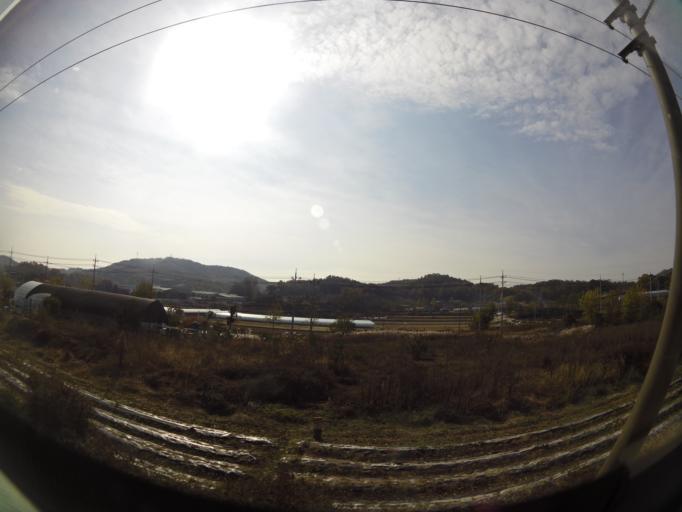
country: KR
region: Daejeon
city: Songgang-dong
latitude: 36.5370
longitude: 127.3452
